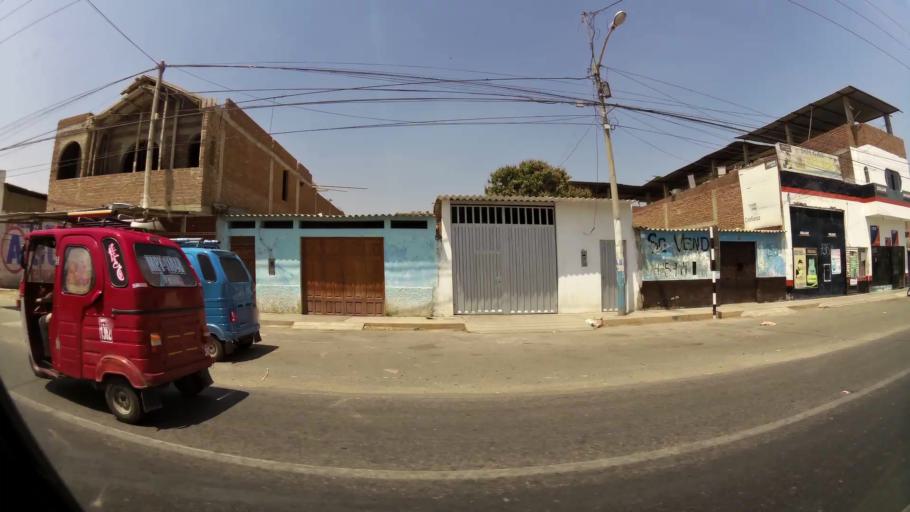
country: PE
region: La Libertad
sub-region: Chepen
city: Chepen
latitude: -7.2120
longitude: -79.4279
